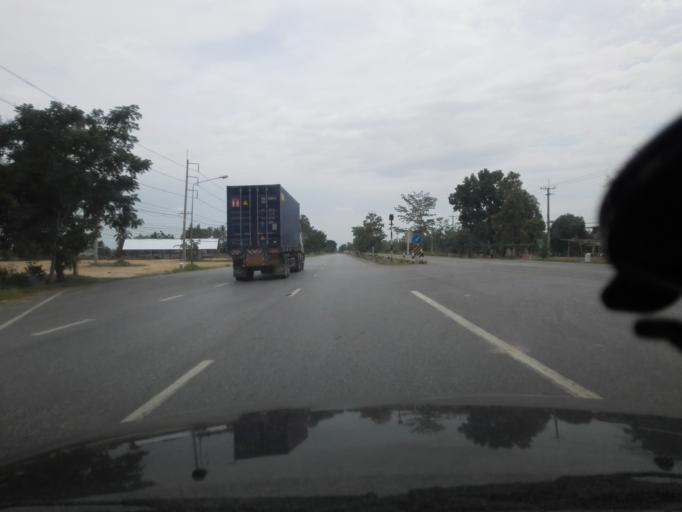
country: TH
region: Kamphaeng Phet
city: Khlong Khlung
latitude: 16.1085
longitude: 99.7190
